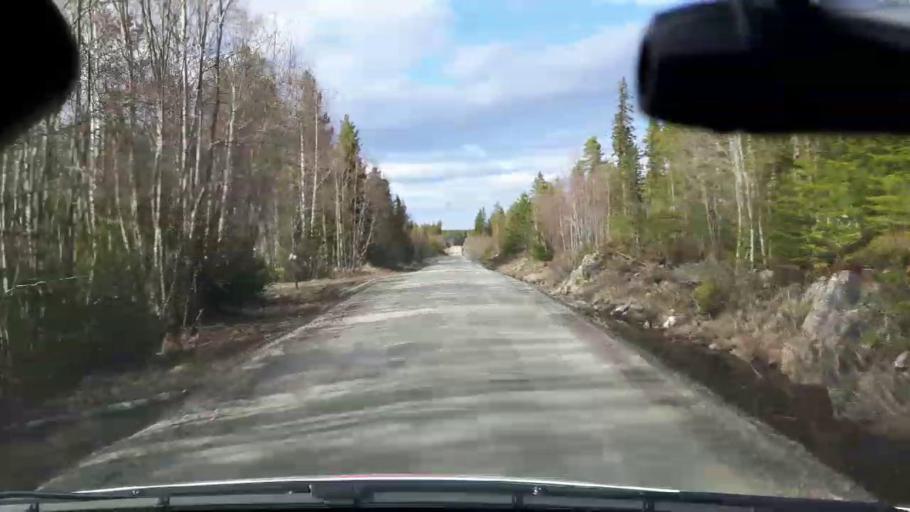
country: SE
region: Jaemtland
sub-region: Bergs Kommun
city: Hoverberg
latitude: 62.9141
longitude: 14.6365
